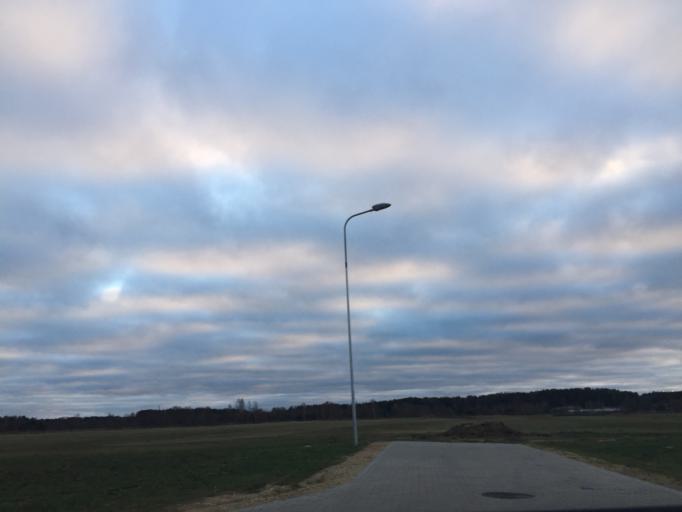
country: LV
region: Adazi
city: Adazi
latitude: 57.0665
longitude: 24.3441
